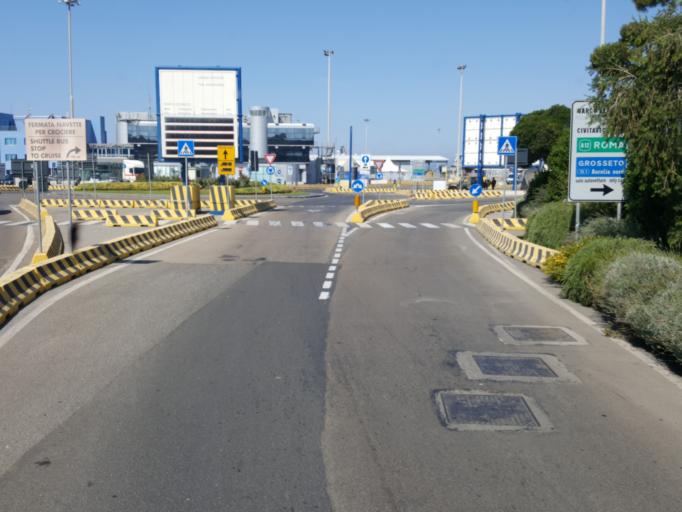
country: IT
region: Latium
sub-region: Citta metropolitana di Roma Capitale
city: Civitavecchia
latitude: 42.0963
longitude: 11.7874
